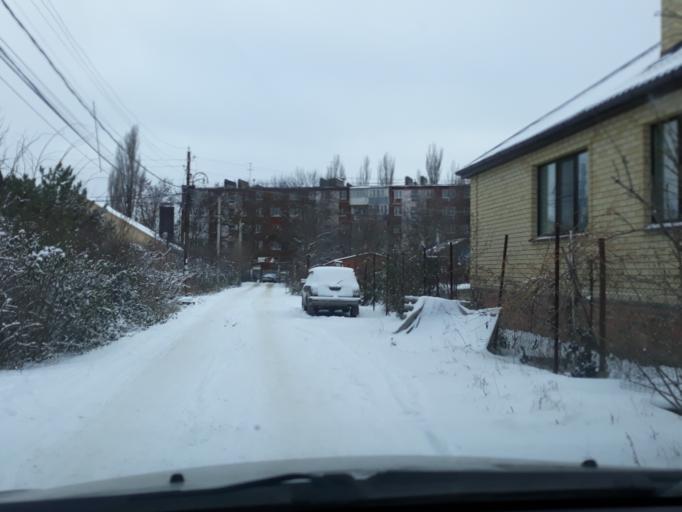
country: RU
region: Rostov
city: Taganrog
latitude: 47.2401
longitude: 38.8722
